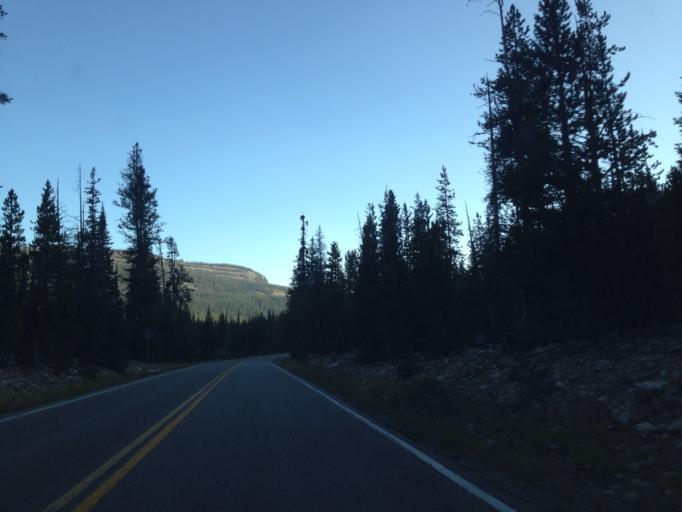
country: US
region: Utah
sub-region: Summit County
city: Kamas
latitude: 40.6458
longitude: -110.9469
